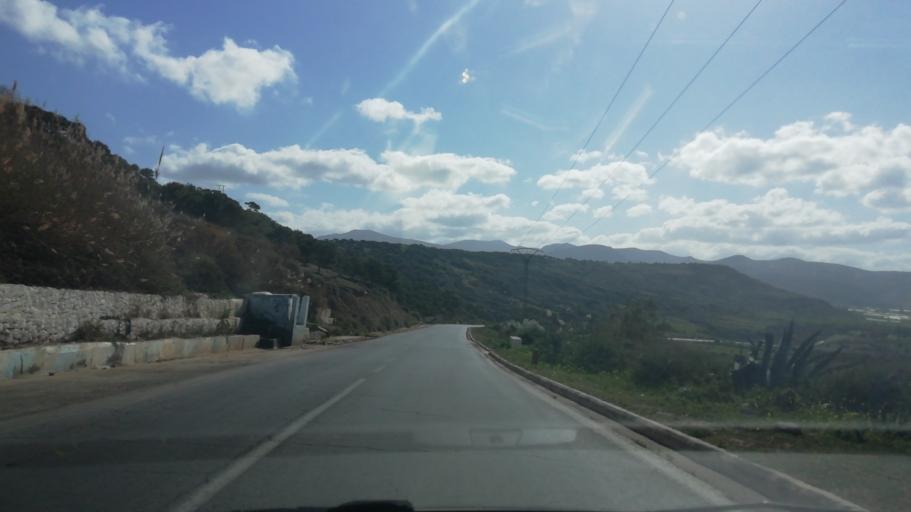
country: DZ
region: Relizane
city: Mazouna
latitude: 36.3095
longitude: 0.6664
